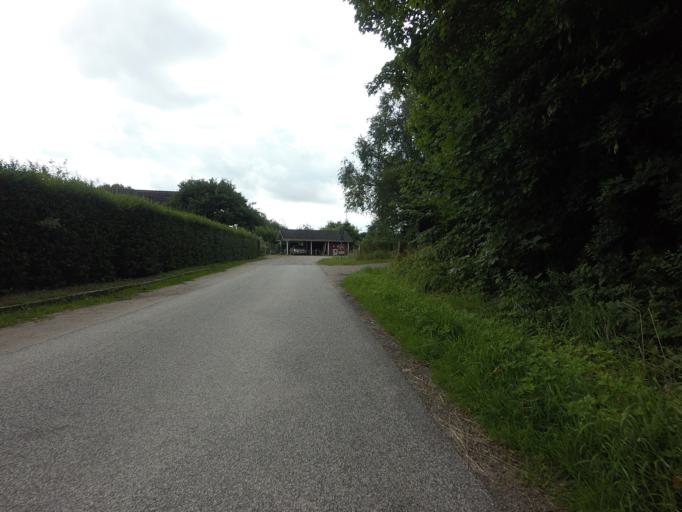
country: DK
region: Central Jutland
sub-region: Randers Kommune
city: Langa
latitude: 56.3859
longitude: 9.8990
